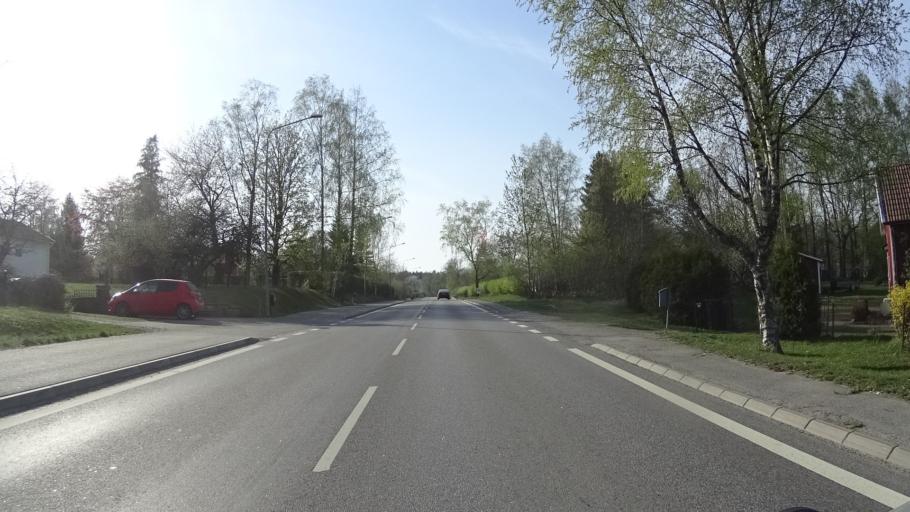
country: SE
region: Vaestra Goetaland
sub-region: Gotene Kommun
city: Goetene
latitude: 58.6294
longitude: 13.4470
